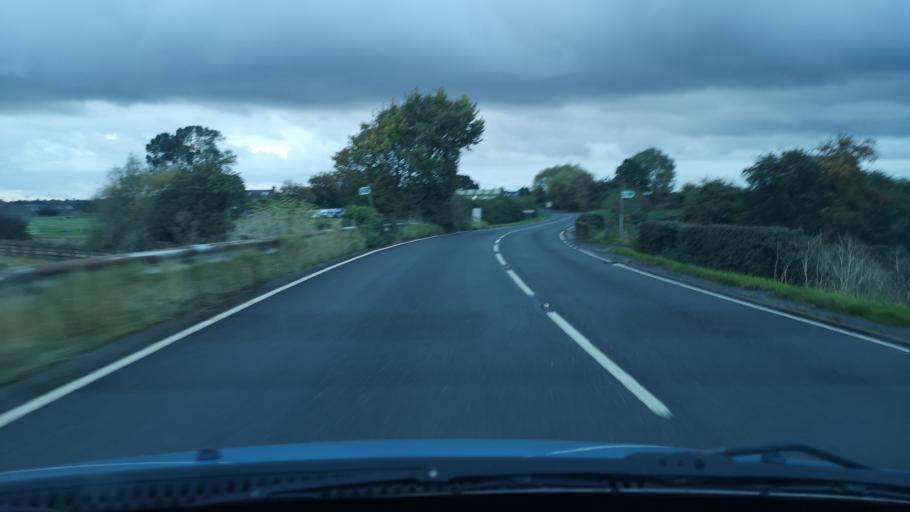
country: GB
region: England
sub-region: City and Borough of Wakefield
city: Badsworth
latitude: 53.6447
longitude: -1.2842
